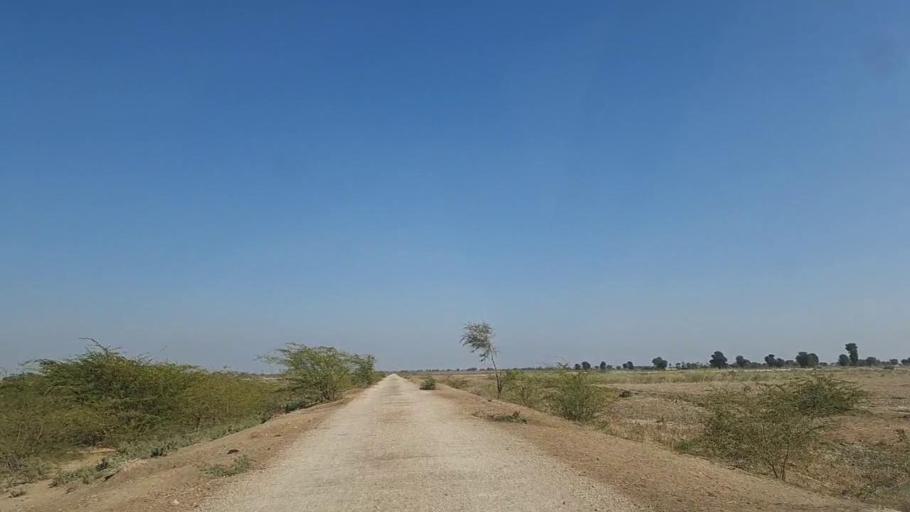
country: PK
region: Sindh
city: Samaro
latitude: 25.3991
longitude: 69.4144
